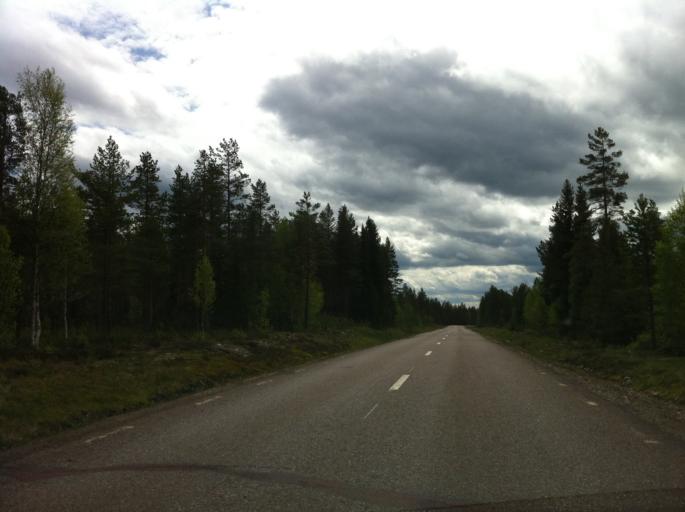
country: NO
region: Hedmark
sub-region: Trysil
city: Innbygda
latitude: 61.5346
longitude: 13.0819
